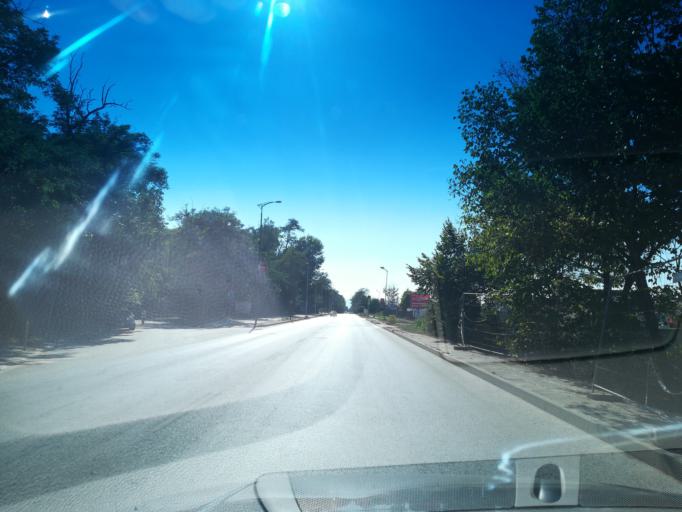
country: BG
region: Plovdiv
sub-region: Obshtina Plovdiv
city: Plovdiv
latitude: 42.1552
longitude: 24.7088
